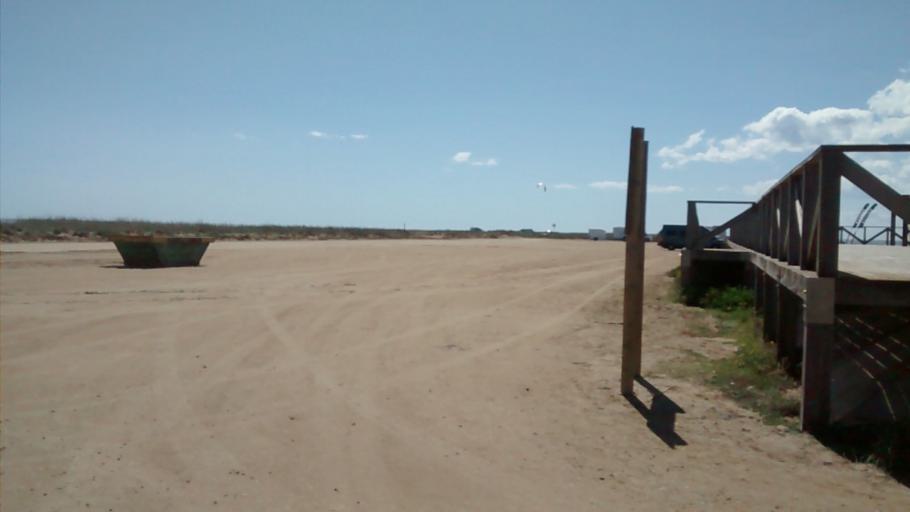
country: ES
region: Catalonia
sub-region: Provincia de Tarragona
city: Deltebre
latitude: 40.6298
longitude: 0.7421
